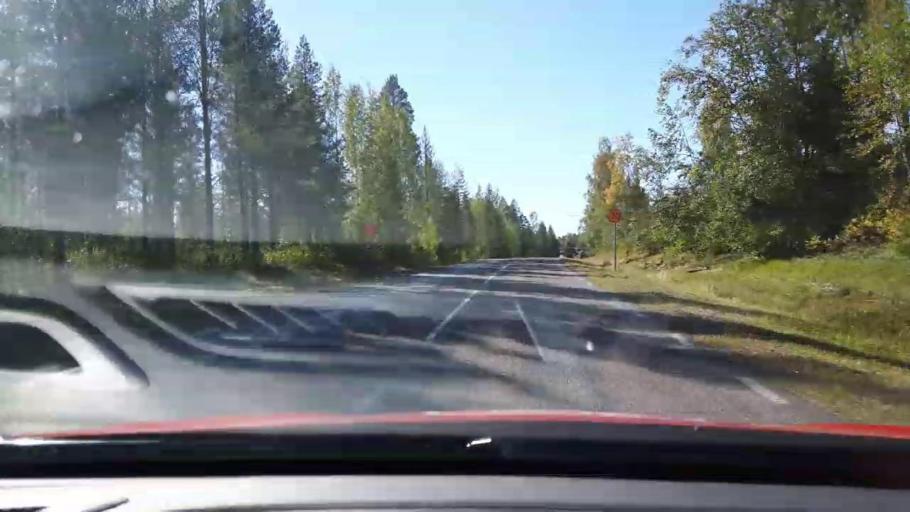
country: SE
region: Jaemtland
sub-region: Harjedalens Kommun
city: Sveg
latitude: 62.1296
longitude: 14.1657
